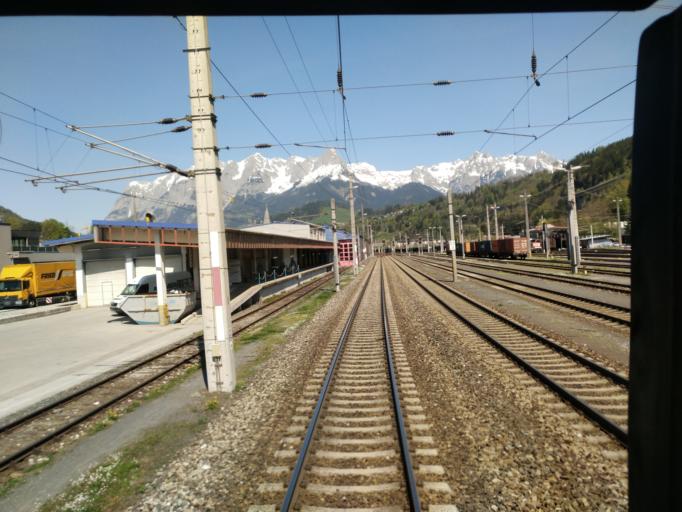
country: AT
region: Salzburg
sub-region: Politischer Bezirk Sankt Johann im Pongau
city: Bischofshofen
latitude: 47.4103
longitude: 13.2182
